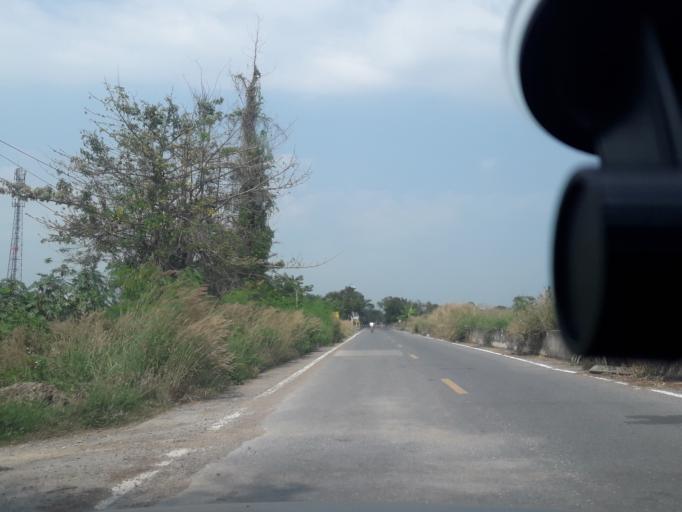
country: TH
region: Sara Buri
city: Nong Khae
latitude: 14.2727
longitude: 100.8912
